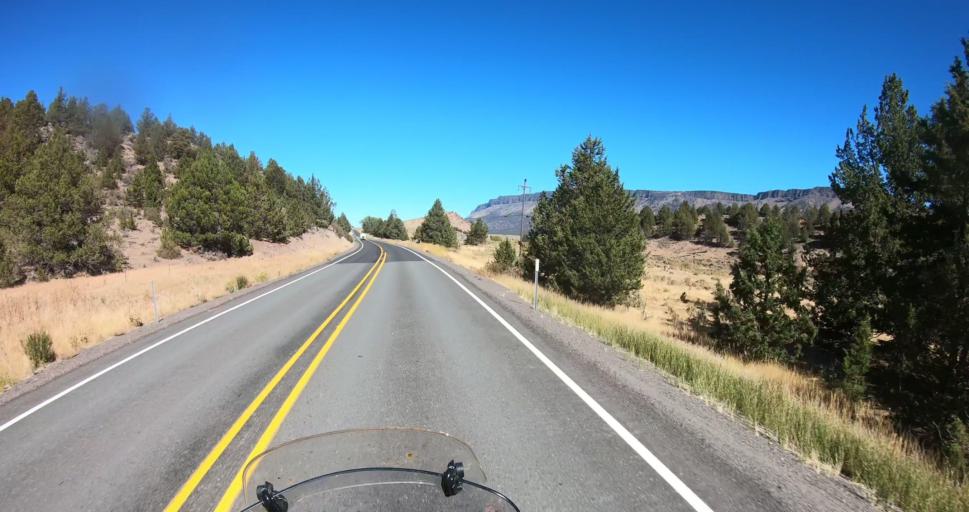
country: US
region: Oregon
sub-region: Lake County
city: Lakeview
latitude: 42.4296
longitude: -120.2828
